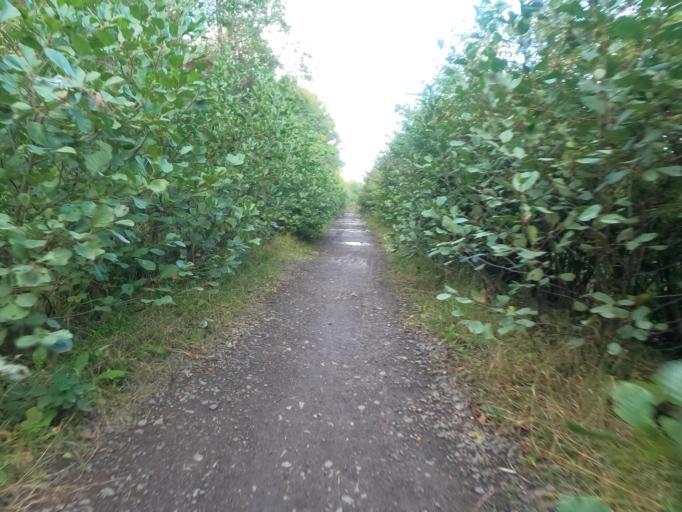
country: GB
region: England
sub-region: Northumberland
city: Seghill
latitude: 55.0719
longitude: -1.5482
